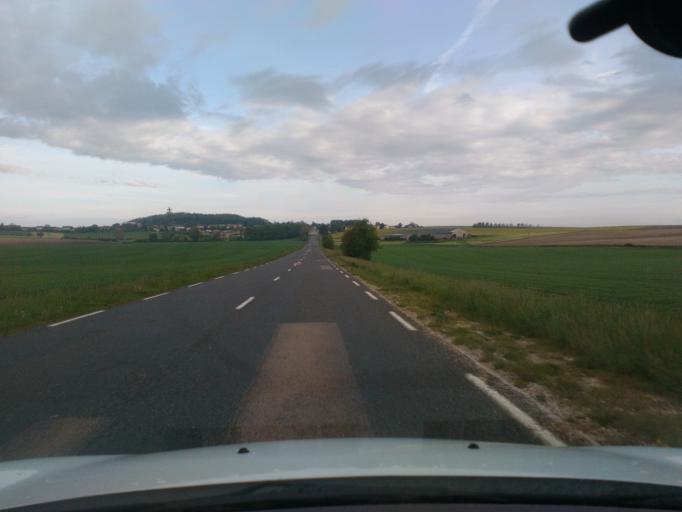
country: FR
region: Champagne-Ardenne
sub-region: Departement de la Haute-Marne
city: Lavilleneuve-au-Roi
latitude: 48.2176
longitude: 4.9048
